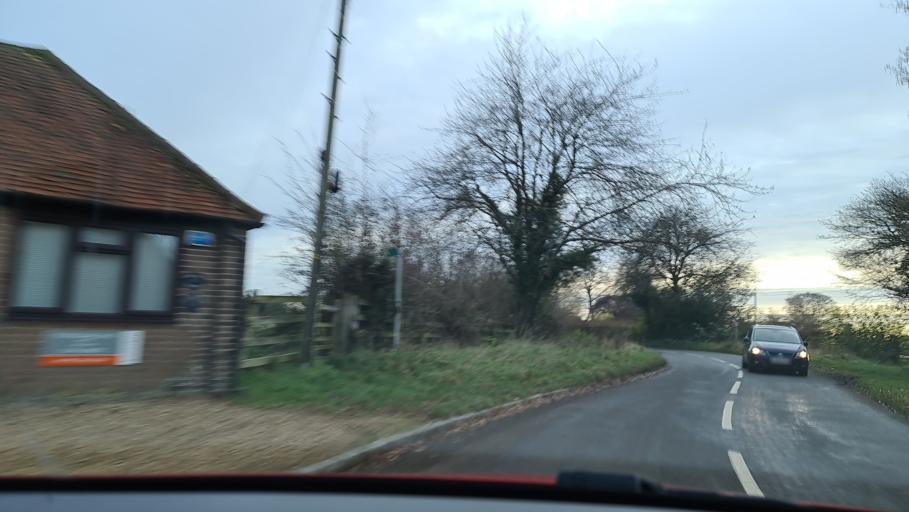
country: GB
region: England
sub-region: Buckinghamshire
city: Princes Risborough
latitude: 51.7077
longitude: -0.7753
